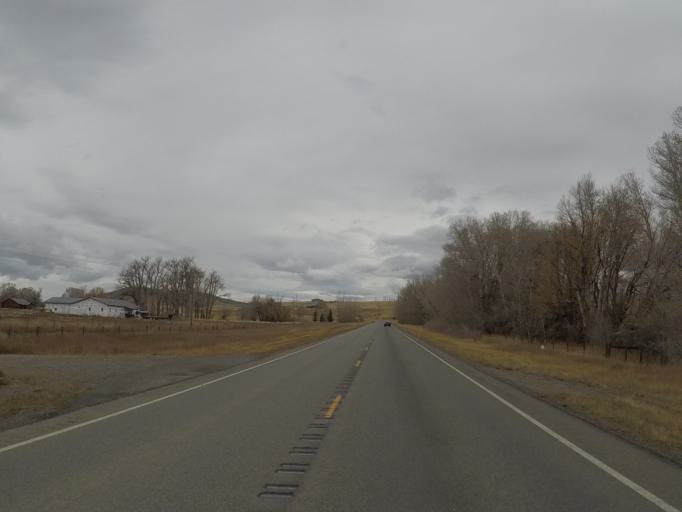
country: US
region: Montana
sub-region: Sweet Grass County
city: Big Timber
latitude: 45.8599
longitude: -109.9393
